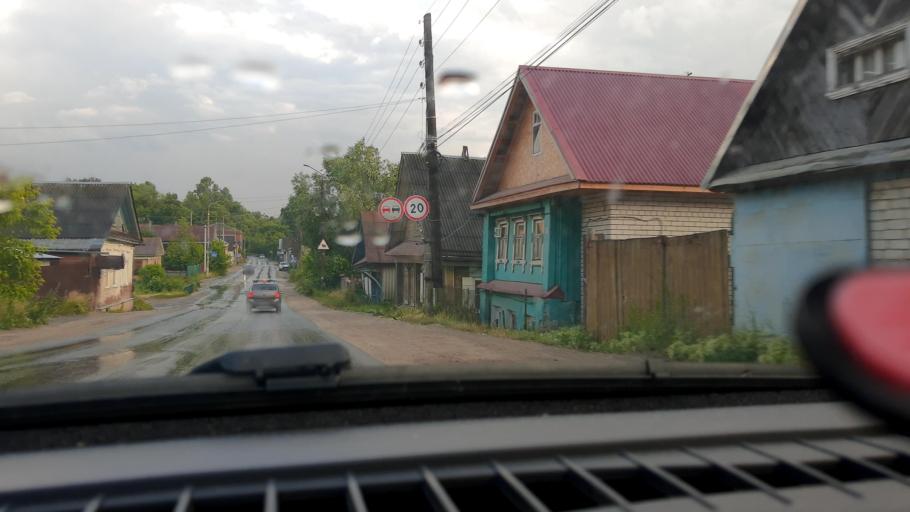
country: RU
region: Nizjnij Novgorod
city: Gorodets
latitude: 56.6526
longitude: 43.4648
